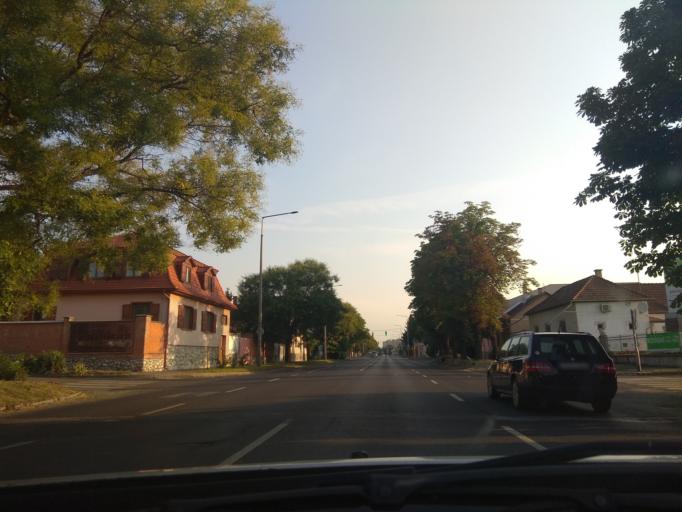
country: HU
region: Borsod-Abauj-Zemplen
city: Miskolc
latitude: 48.0914
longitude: 20.7922
